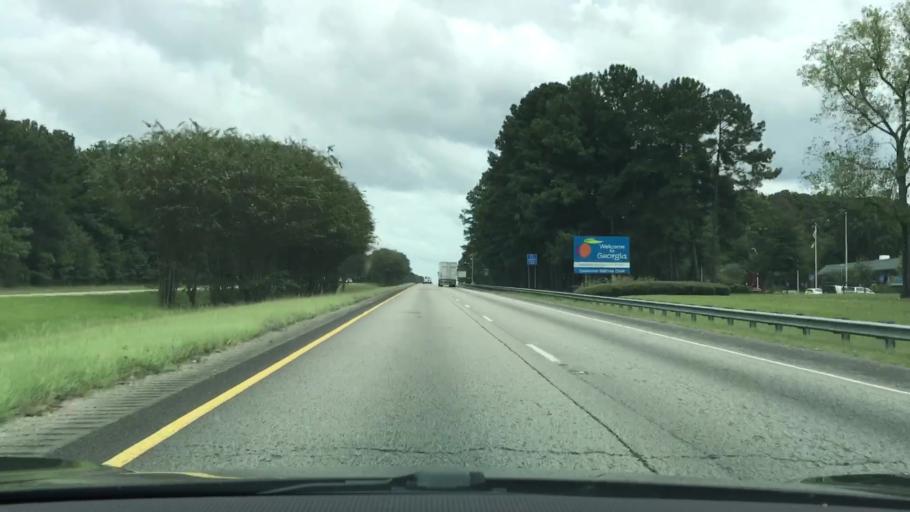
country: US
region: Alabama
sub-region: Chambers County
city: Lanett
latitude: 32.8591
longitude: -85.1740
